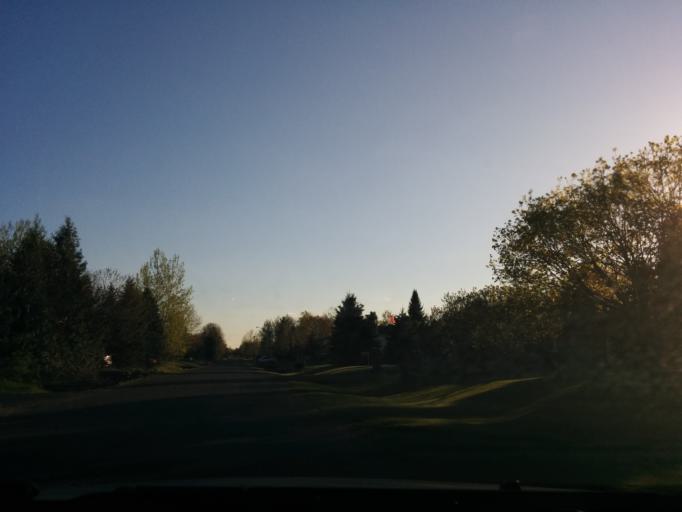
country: CA
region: Ontario
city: Ottawa
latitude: 45.1490
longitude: -75.5955
